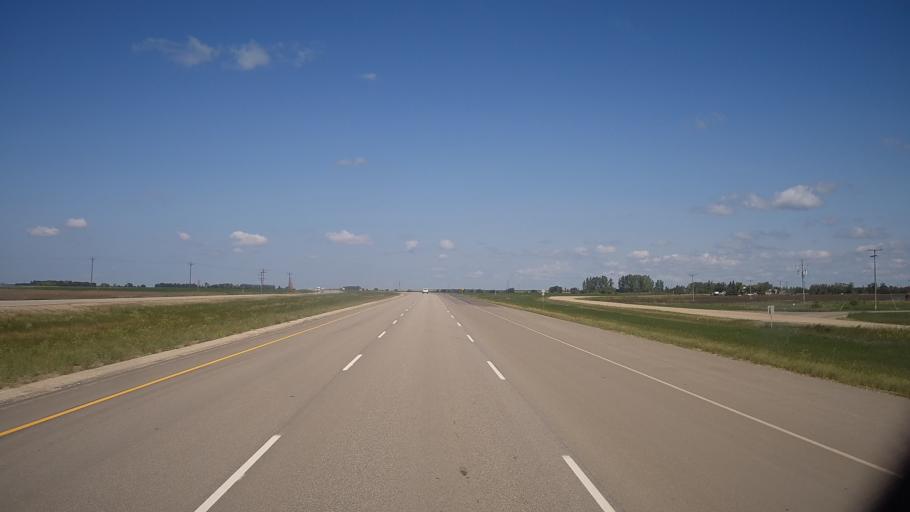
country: CA
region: Saskatchewan
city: Saskatoon
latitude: 52.0568
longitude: -106.4781
